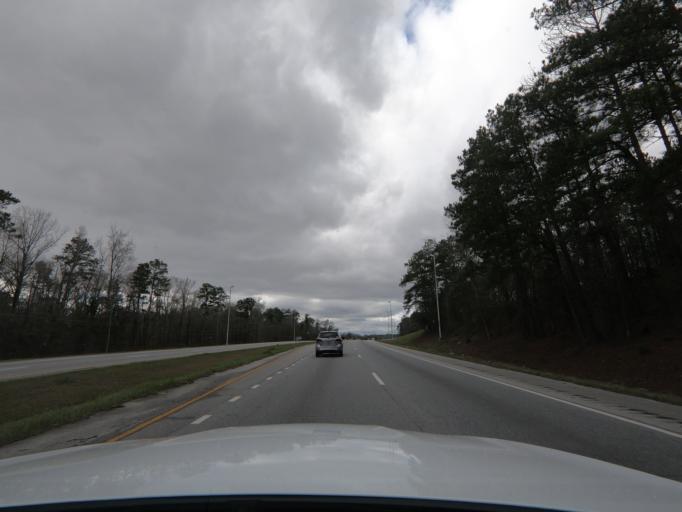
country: US
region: Alabama
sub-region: Russell County
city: Phenix City
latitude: 32.4322
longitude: -85.0276
